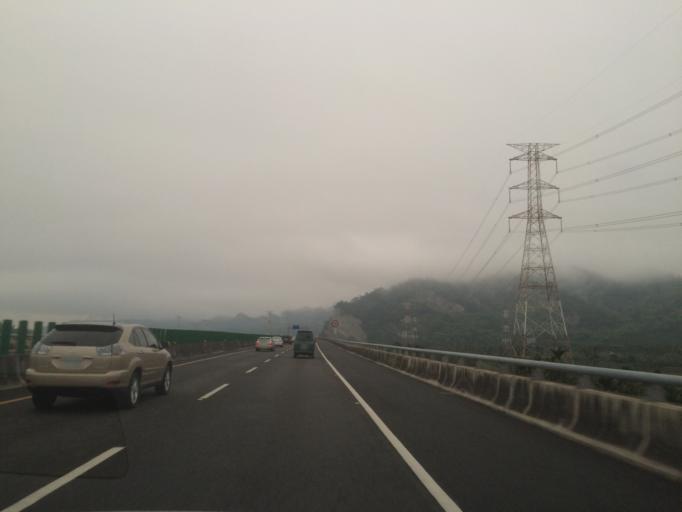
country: TW
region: Taiwan
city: Zhongxing New Village
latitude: 23.9892
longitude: 120.7549
